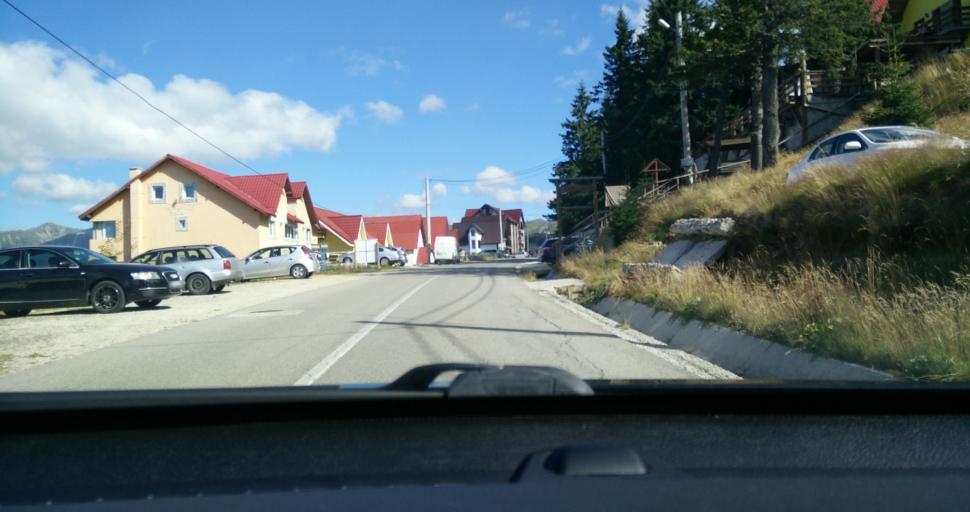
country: RO
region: Gorj
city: Novaci-Straini
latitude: 45.2781
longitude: 23.6887
